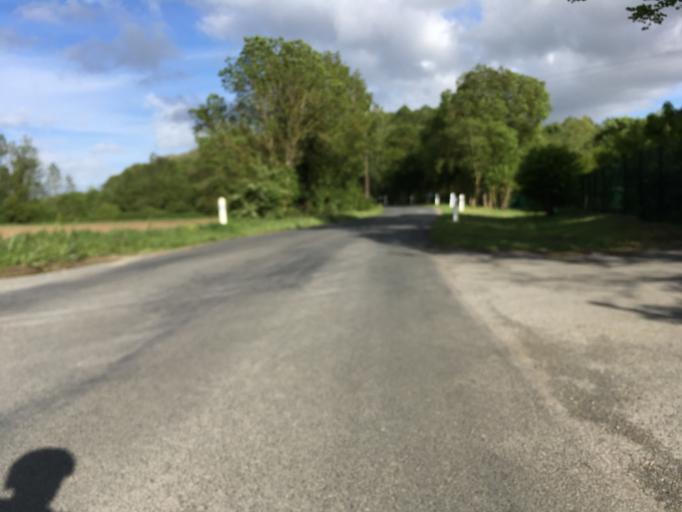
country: FR
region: Poitou-Charentes
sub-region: Departement de la Charente-Maritime
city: Verines
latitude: 46.1786
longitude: -0.9248
